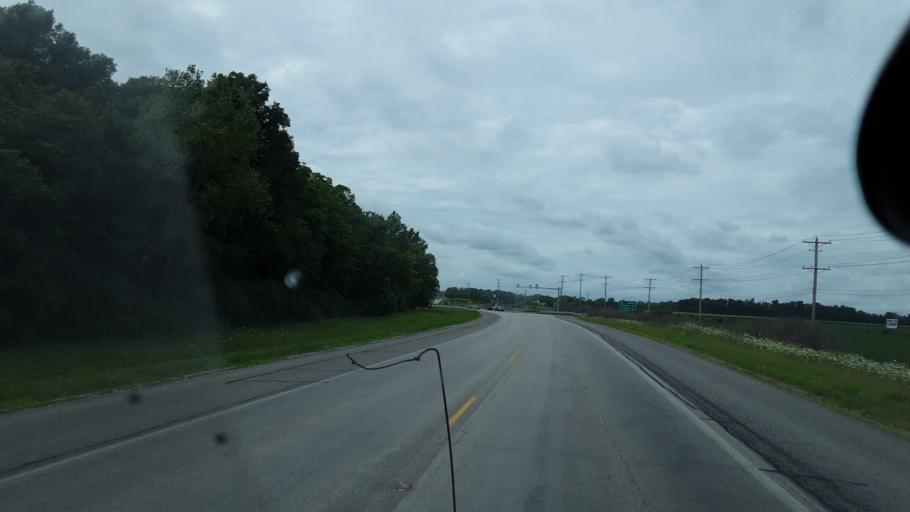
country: US
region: Indiana
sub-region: Adams County
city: Decatur
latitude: 40.8031
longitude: -84.9325
